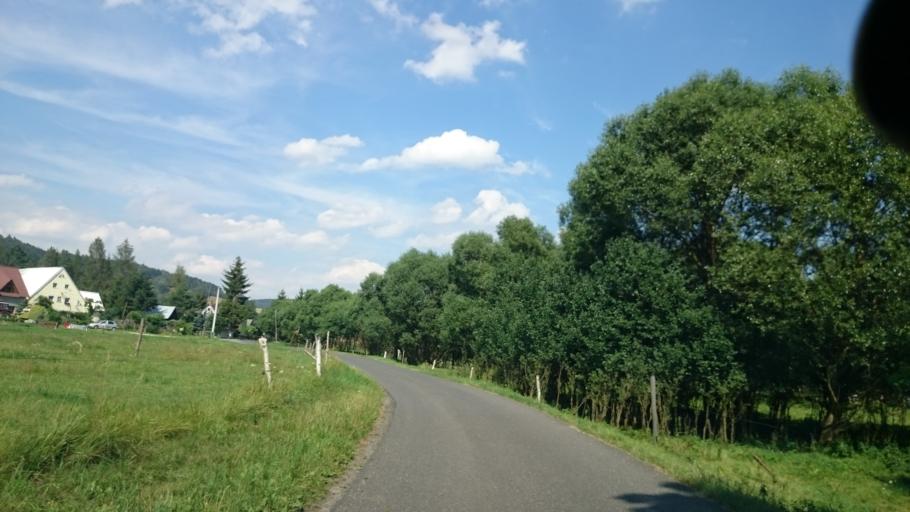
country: PL
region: Lower Silesian Voivodeship
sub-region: Powiat klodzki
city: Ladek-Zdroj
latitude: 50.3492
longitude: 16.8281
